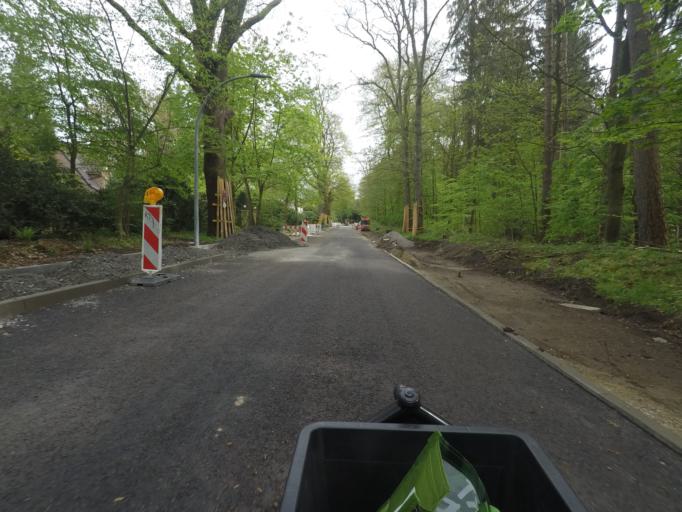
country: DE
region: Hamburg
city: Bergstedt
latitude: 53.6423
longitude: 10.1691
